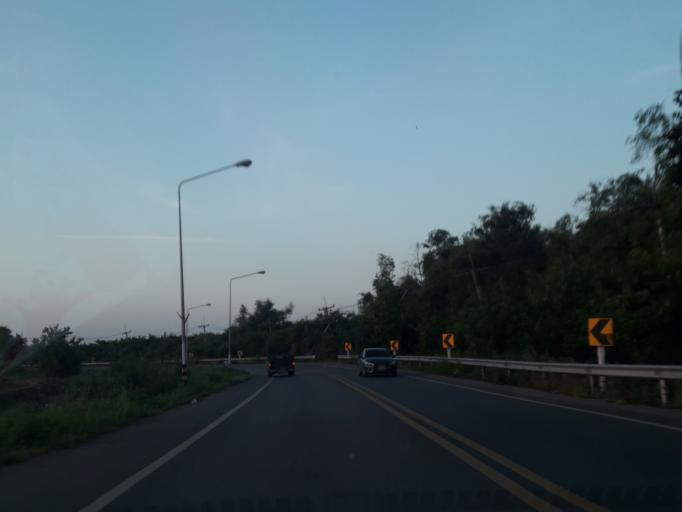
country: TH
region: Phra Nakhon Si Ayutthaya
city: Maha Rat
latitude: 14.5580
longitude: 100.5395
